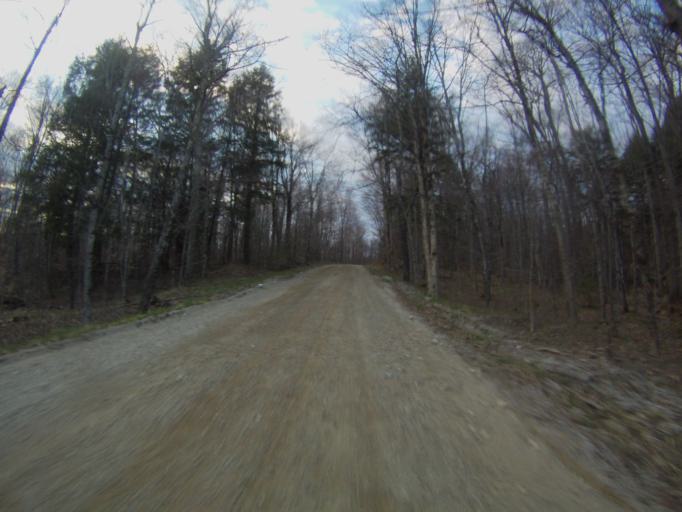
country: US
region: Vermont
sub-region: Rutland County
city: Brandon
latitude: 43.9185
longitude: -73.0182
